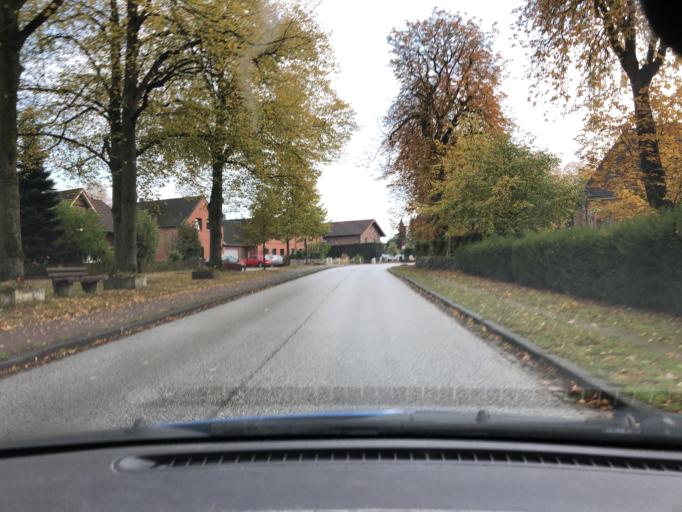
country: DE
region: Schleswig-Holstein
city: Siek
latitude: 53.6350
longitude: 10.2976
